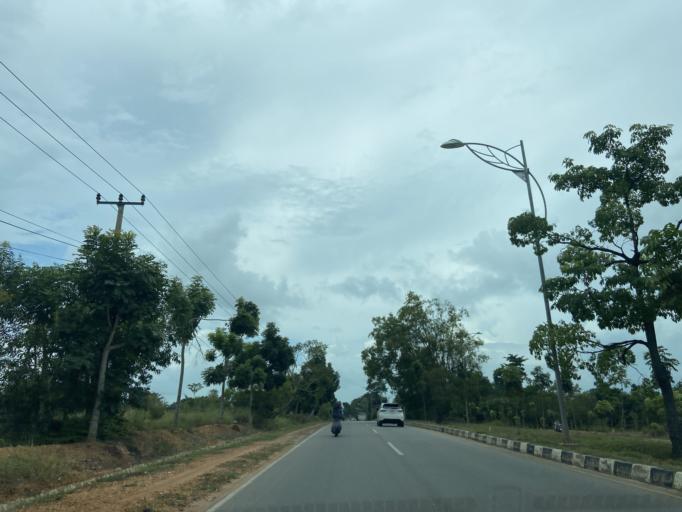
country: SG
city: Singapore
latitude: 1.1443
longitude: 104.1263
